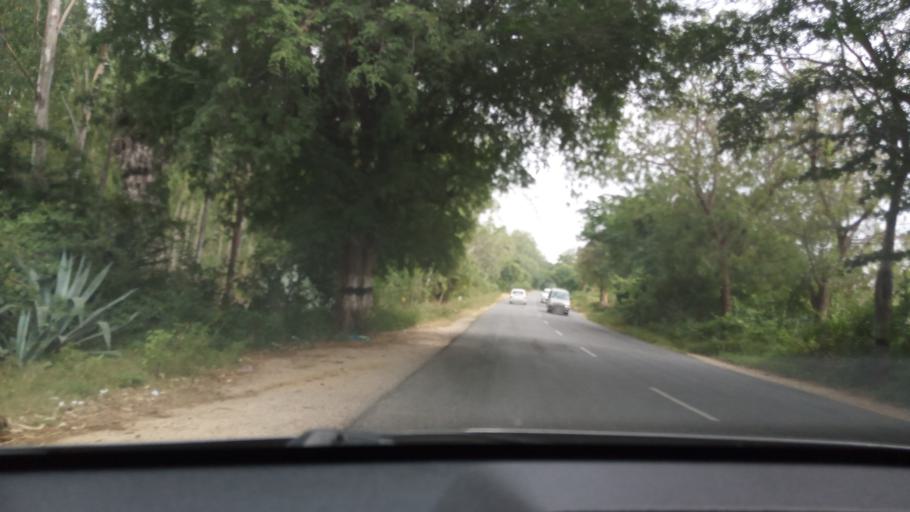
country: IN
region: Andhra Pradesh
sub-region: Chittoor
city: Pakala
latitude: 13.6563
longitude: 78.8479
